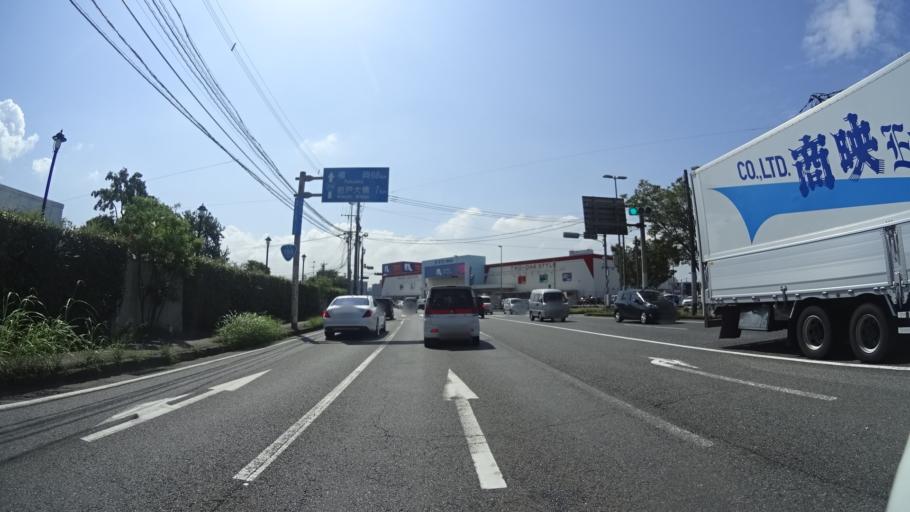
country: JP
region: Yamaguchi
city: Shimonoseki
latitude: 33.8892
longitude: 130.8968
